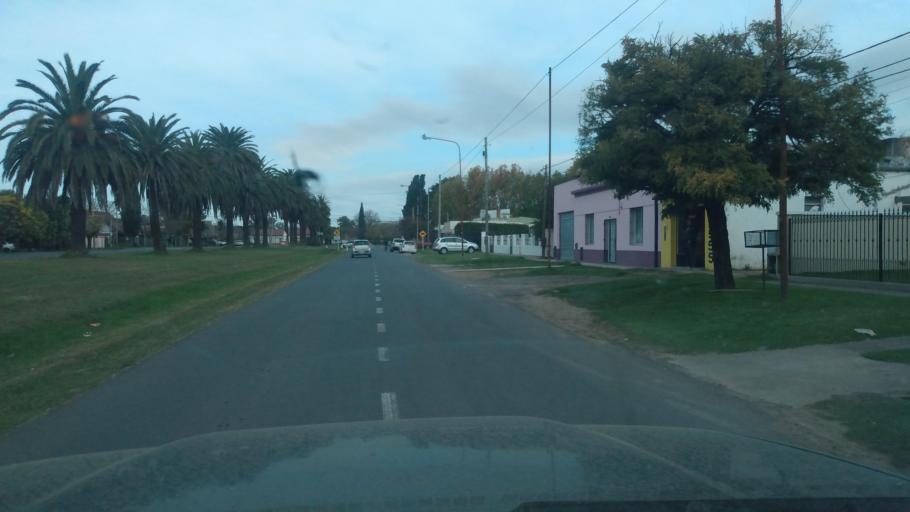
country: AR
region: Buenos Aires
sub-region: Partido de Lujan
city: Lujan
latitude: -34.5982
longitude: -59.1758
